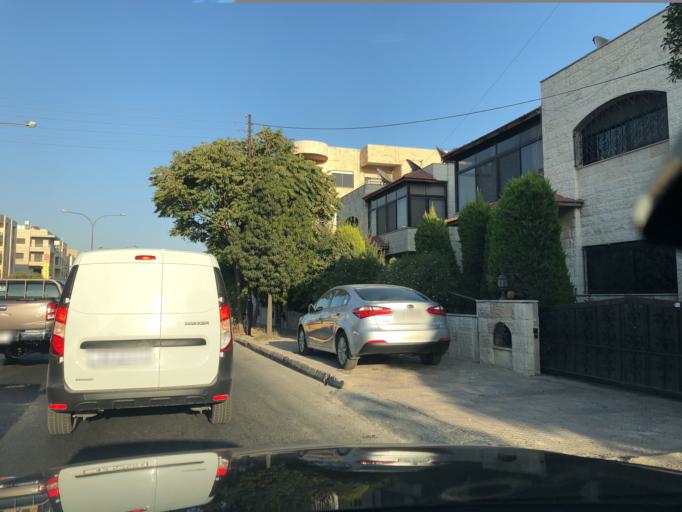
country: JO
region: Amman
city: Wadi as Sir
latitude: 31.9462
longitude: 35.8672
